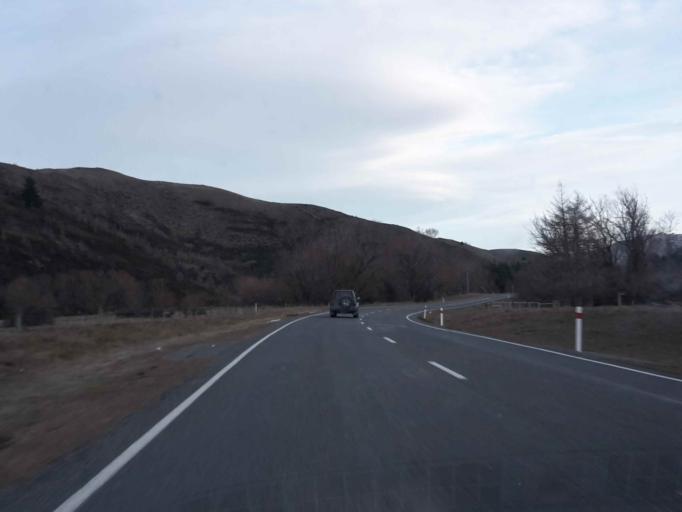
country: NZ
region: Canterbury
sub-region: Timaru District
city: Pleasant Point
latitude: -44.0735
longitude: 170.6667
